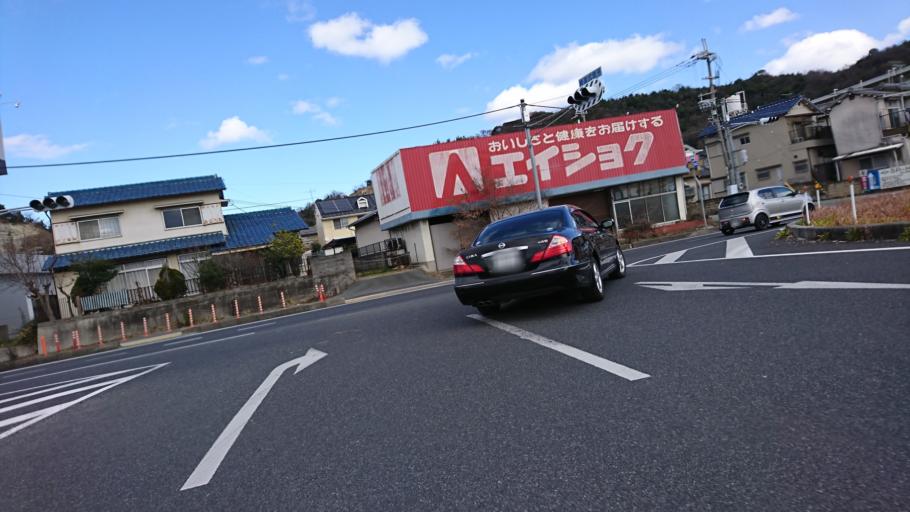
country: JP
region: Hyogo
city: Kakogawacho-honmachi
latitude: 34.7780
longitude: 134.7913
